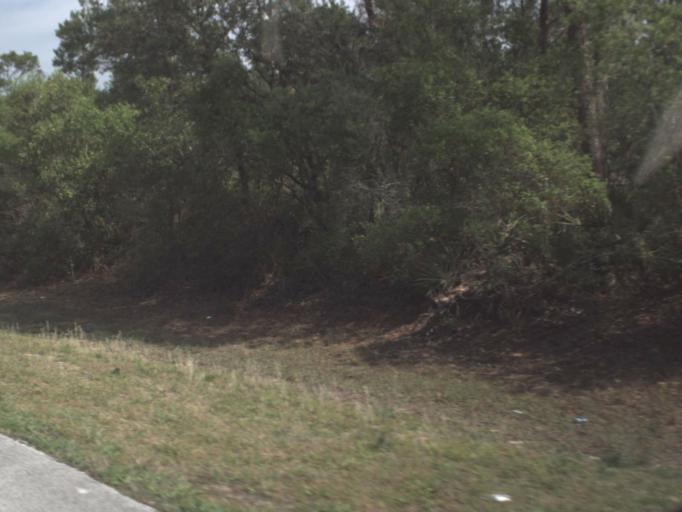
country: US
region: Florida
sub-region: Lake County
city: Astor
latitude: 29.1767
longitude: -81.6477
